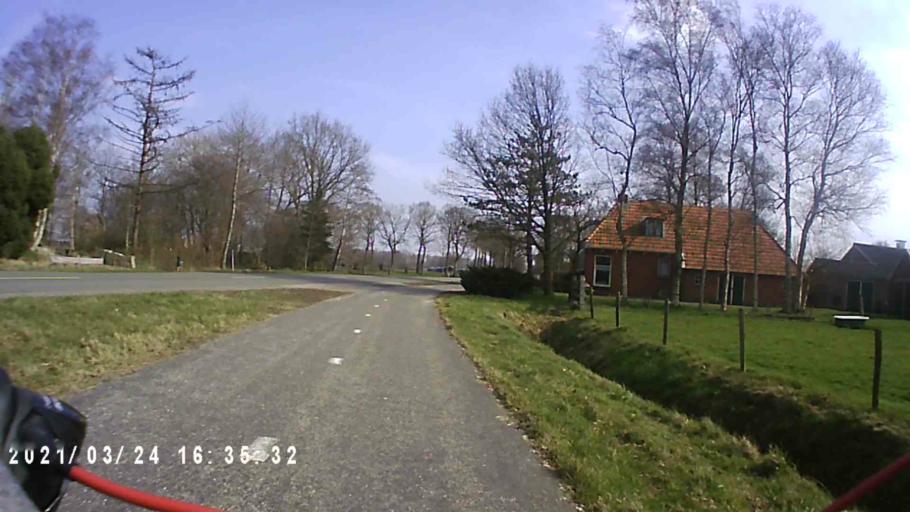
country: NL
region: Groningen
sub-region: Gemeente Leek
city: Leek
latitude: 53.0660
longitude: 6.2747
